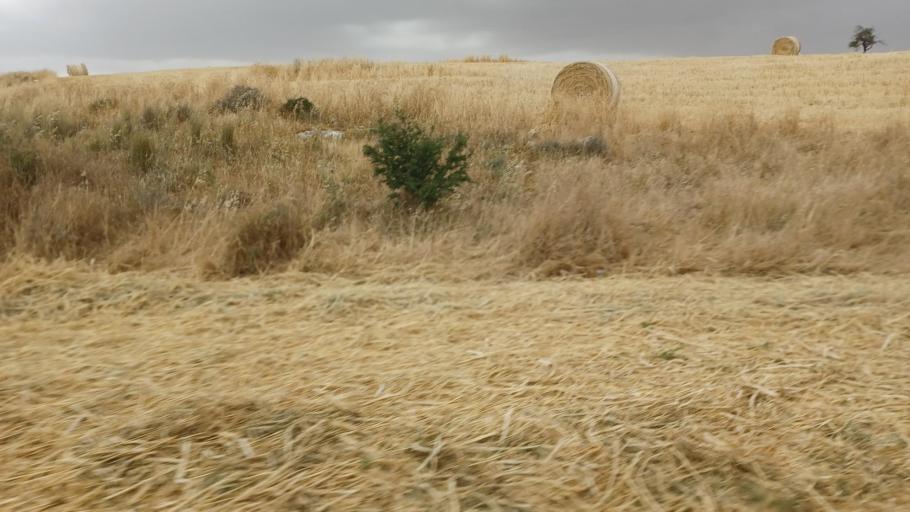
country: CY
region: Larnaka
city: Athienou
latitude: 35.0312
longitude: 33.5681
